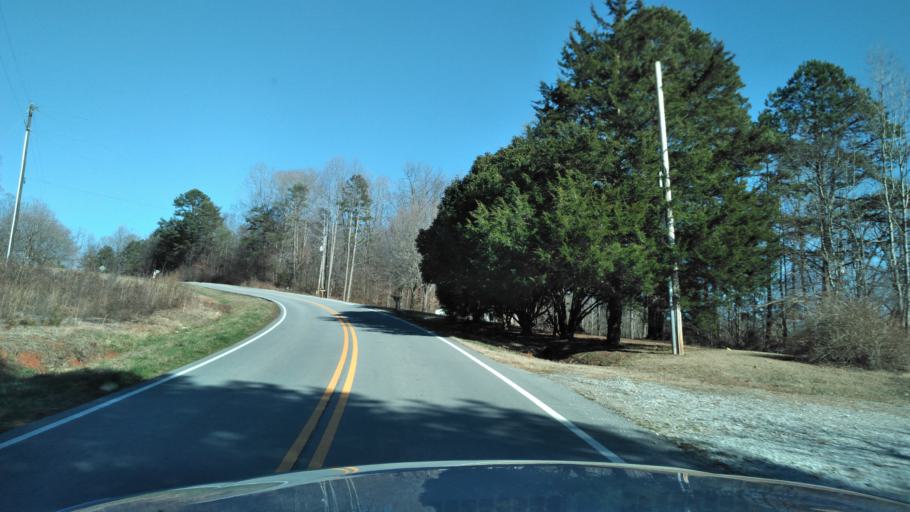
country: US
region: Georgia
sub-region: Hall County
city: Lula
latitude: 34.3122
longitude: -83.7205
